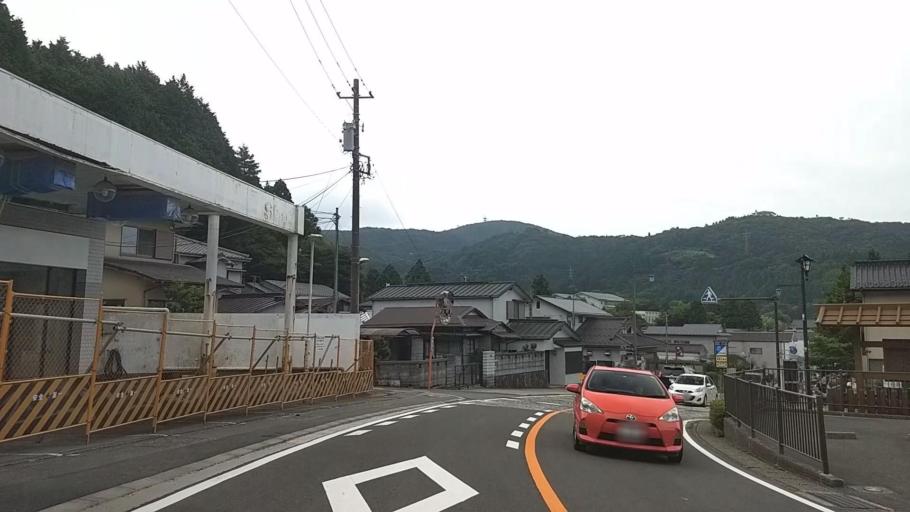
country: JP
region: Kanagawa
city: Hakone
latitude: 35.1918
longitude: 139.0276
